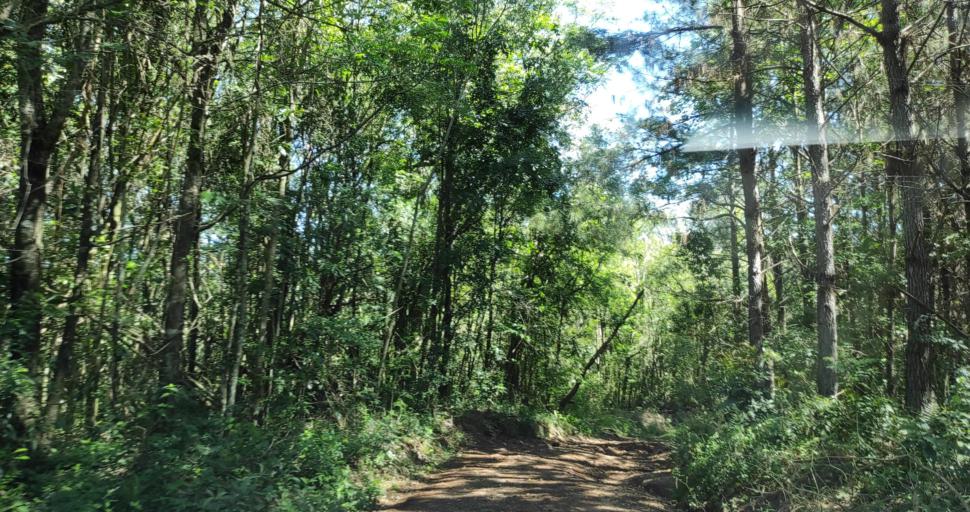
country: AR
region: Misiones
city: Ruiz de Montoya
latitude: -26.9522
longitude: -54.9814
